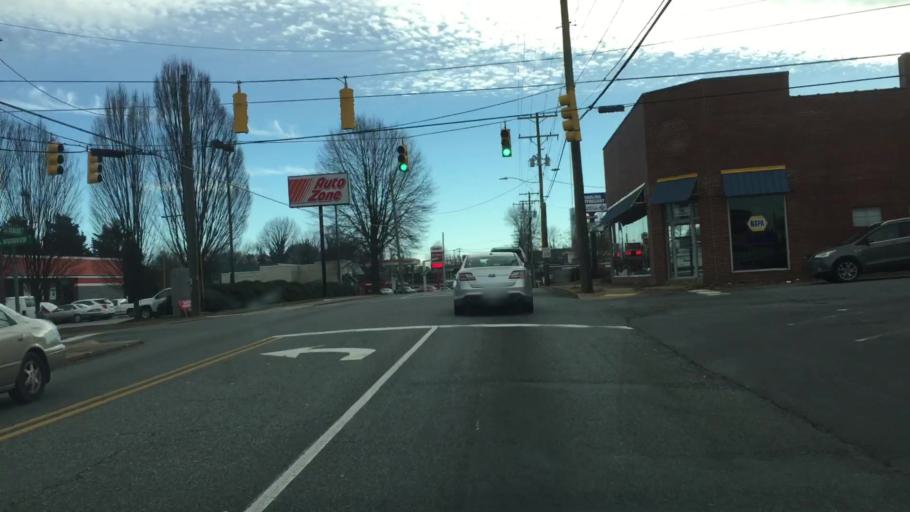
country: US
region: North Carolina
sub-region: Rockingham County
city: Reidsville
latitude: 36.3521
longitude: -79.6648
